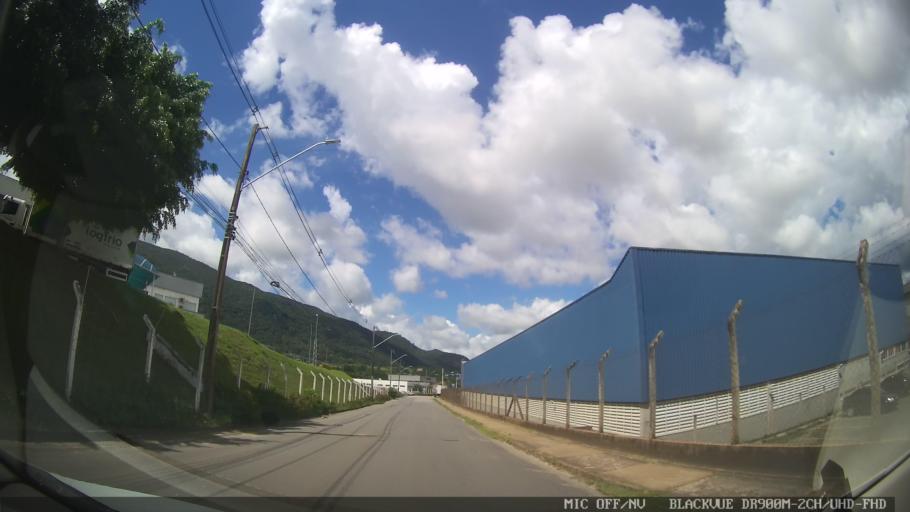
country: BR
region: Minas Gerais
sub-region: Extrema
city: Extrema
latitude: -22.8762
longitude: -46.3498
